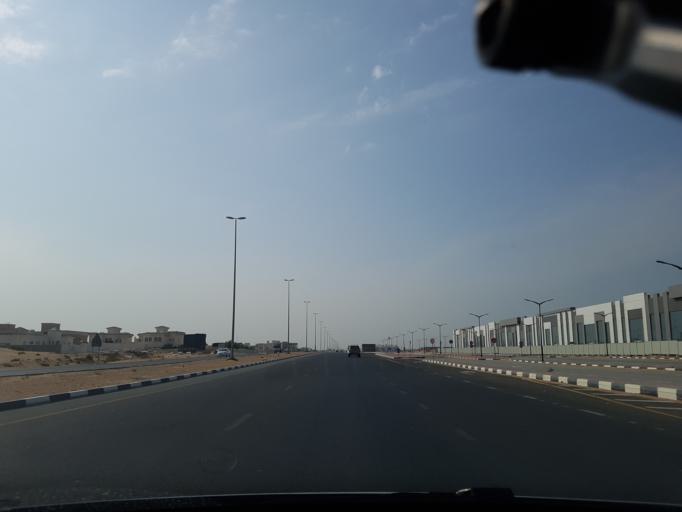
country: AE
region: Ajman
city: Ajman
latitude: 25.4237
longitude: 55.5287
